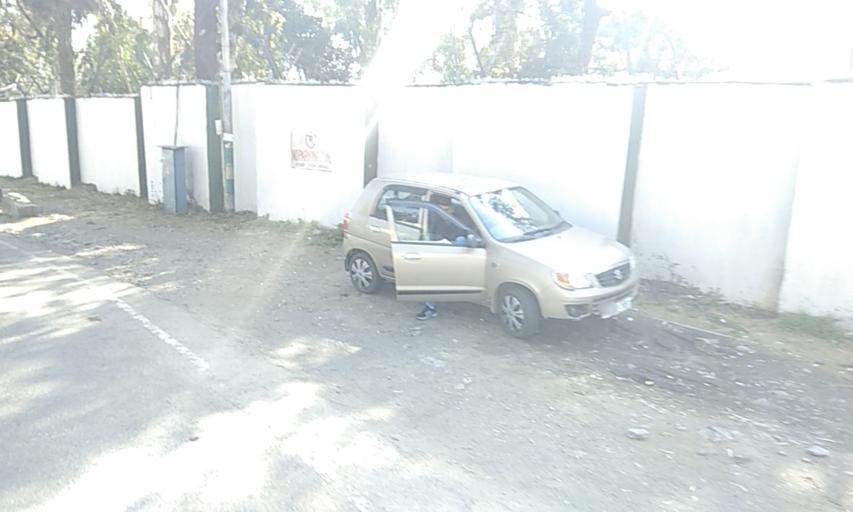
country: IN
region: Himachal Pradesh
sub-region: Kangra
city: Dharmsala
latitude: 32.1783
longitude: 76.3791
